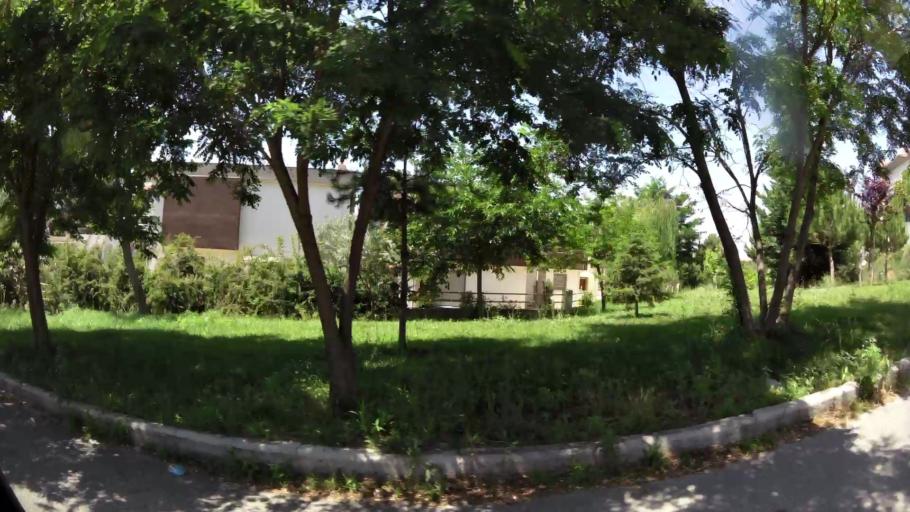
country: GR
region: Central Macedonia
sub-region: Nomos Thessalonikis
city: Trilofos
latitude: 40.4624
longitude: 22.9748
